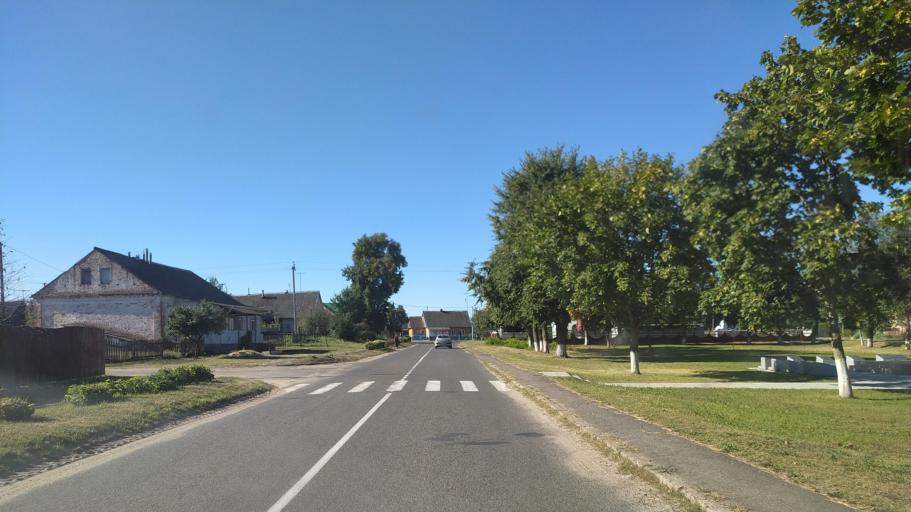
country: BY
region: Brest
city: Pruzhany
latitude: 52.4827
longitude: 24.7046
